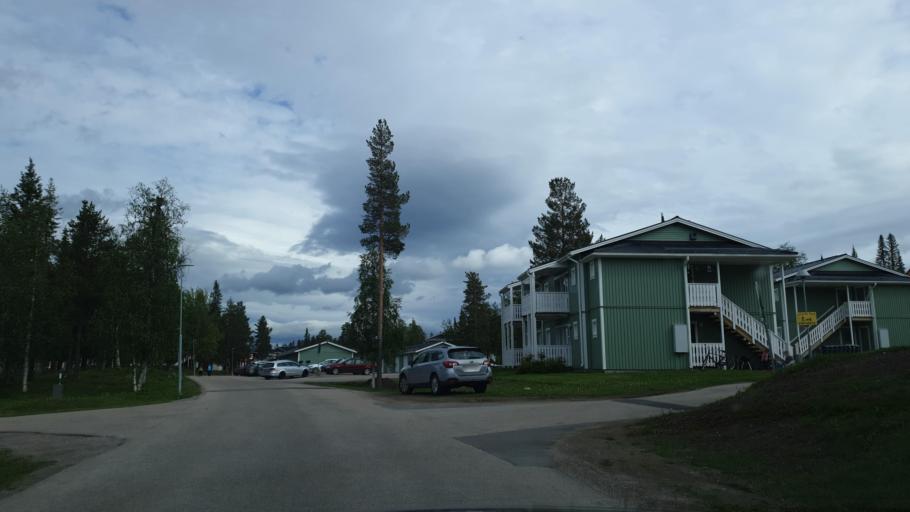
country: SE
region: Norrbotten
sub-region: Gallivare Kommun
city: Gaellivare
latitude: 67.1247
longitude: 20.6570
